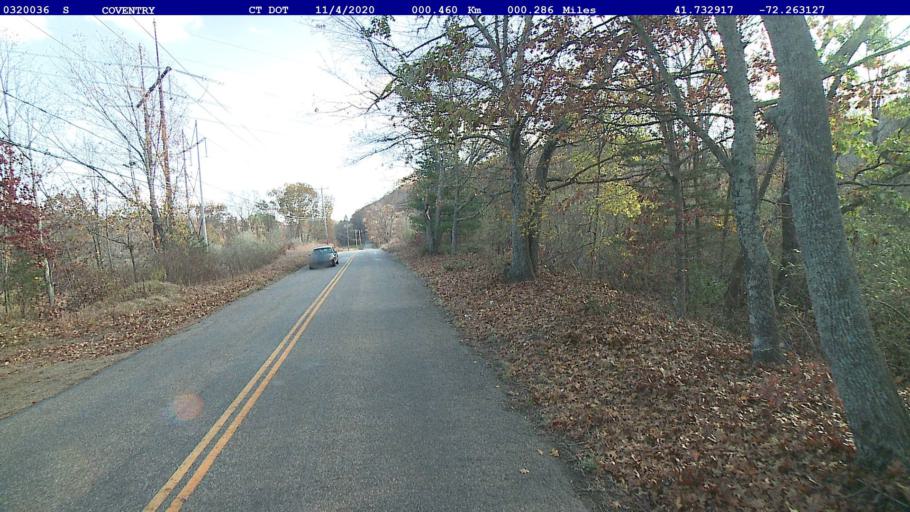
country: US
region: Connecticut
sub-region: Tolland County
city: Mansfield City
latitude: 41.7329
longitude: -72.2631
